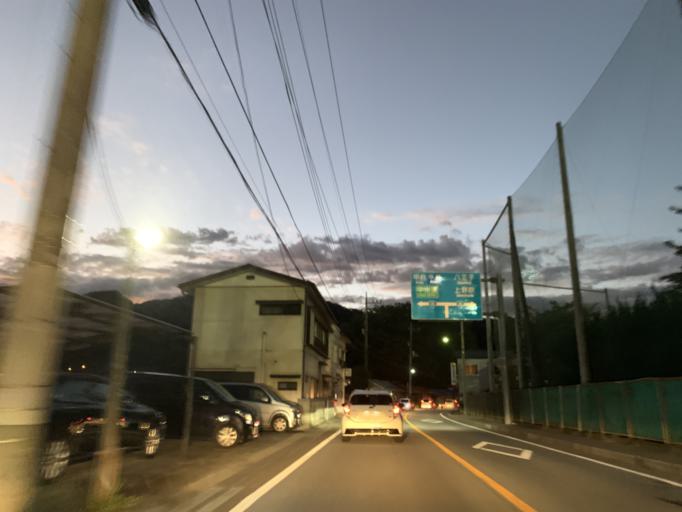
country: JP
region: Yamanashi
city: Otsuki
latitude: 35.6086
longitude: 138.9384
